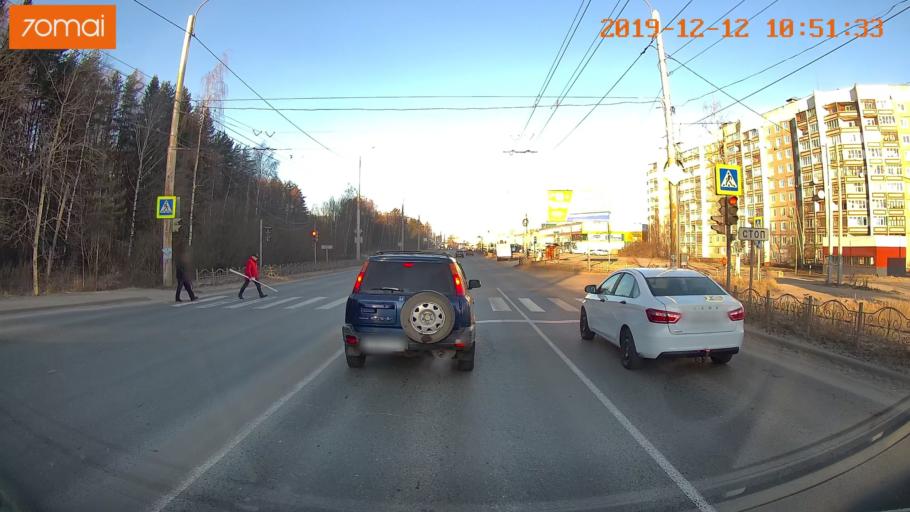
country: RU
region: Ivanovo
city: Kokhma
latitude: 56.9539
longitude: 41.0430
